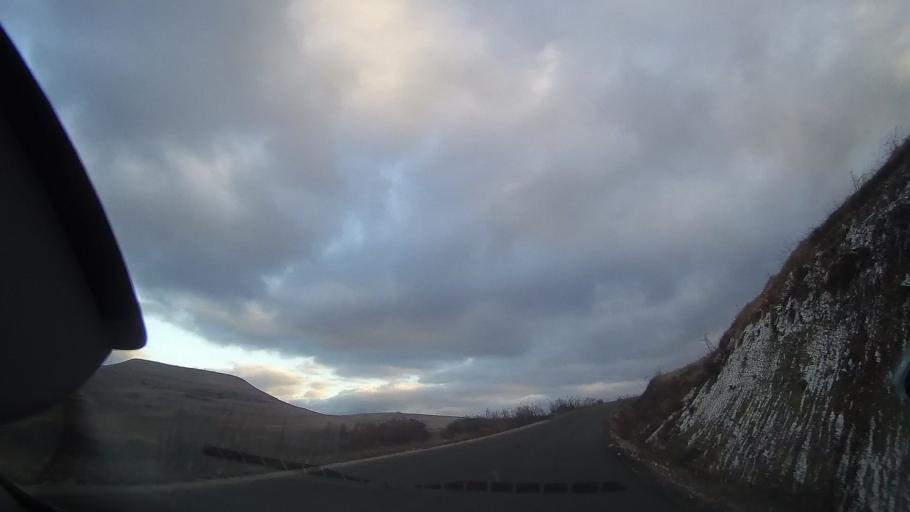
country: RO
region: Cluj
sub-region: Comuna Calatele
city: Calatele
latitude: 46.7829
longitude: 23.0491
